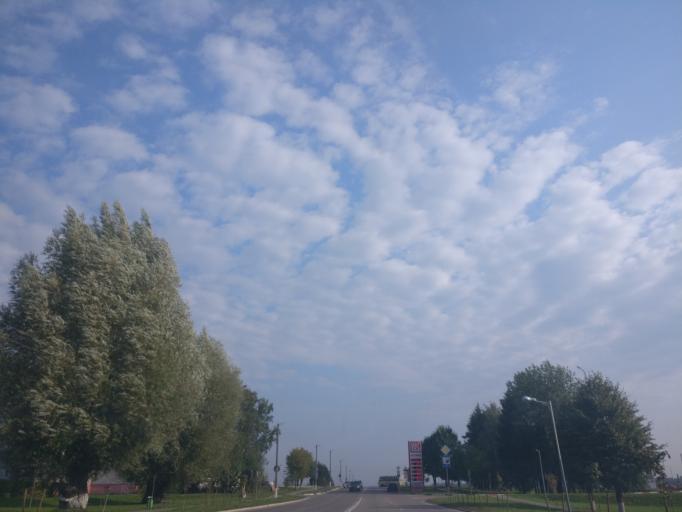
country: BY
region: Minsk
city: Lahoysk
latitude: 54.1931
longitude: 27.8323
